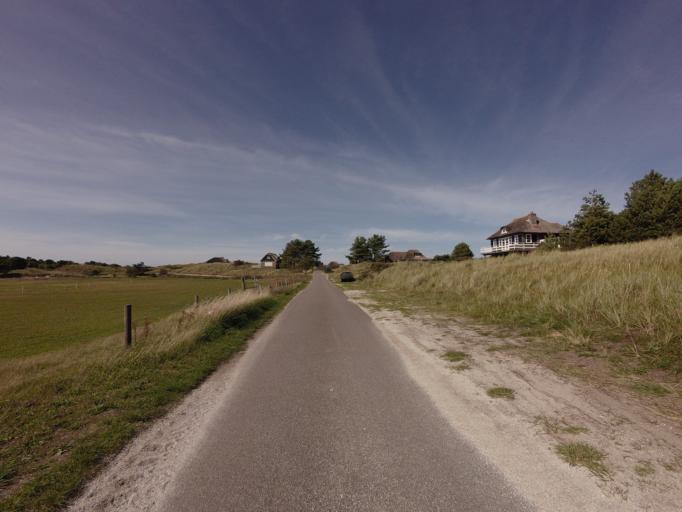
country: NL
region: Friesland
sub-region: Gemeente Ameland
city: Nes
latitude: 53.4533
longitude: 5.7727
